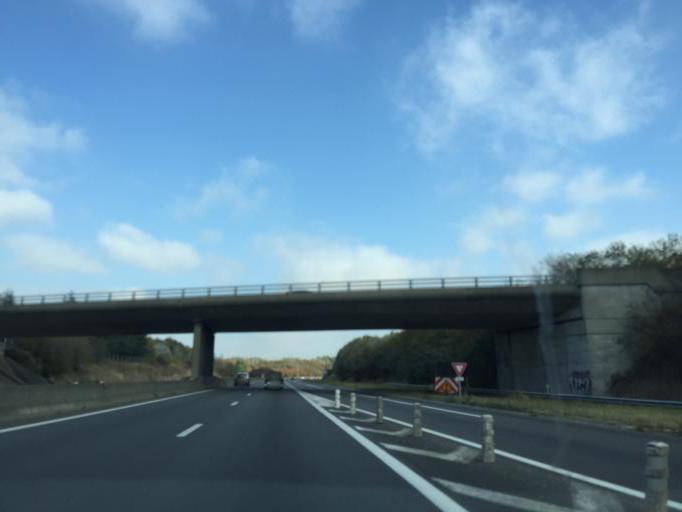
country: FR
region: Rhone-Alpes
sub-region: Departement du Rhone
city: Mions
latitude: 45.6615
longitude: 4.9232
